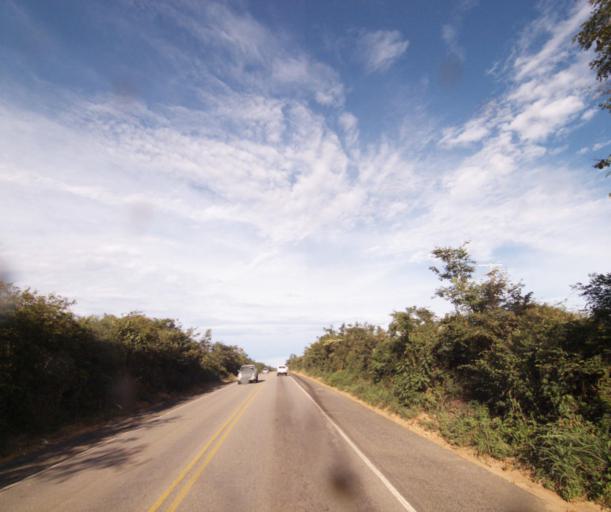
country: BR
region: Bahia
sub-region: Caetite
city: Caetite
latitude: -14.0801
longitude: -42.5557
